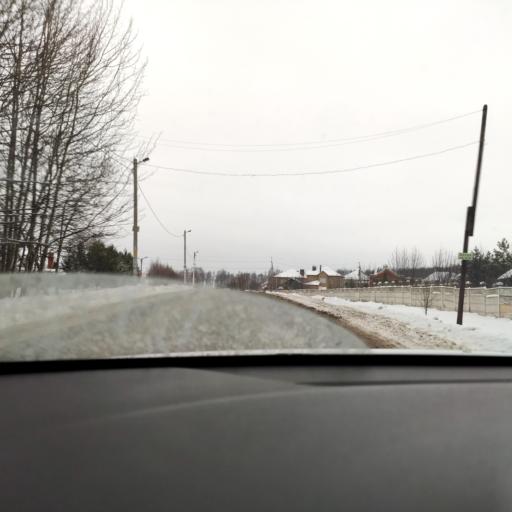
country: RU
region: Tatarstan
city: Osinovo
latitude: 55.8568
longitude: 48.8209
